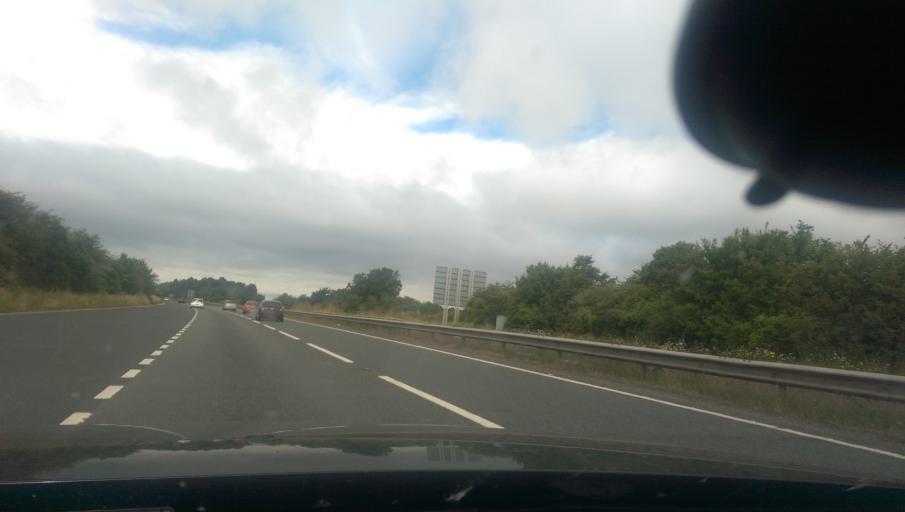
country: GB
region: England
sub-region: Hampshire
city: Abbotts Ann
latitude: 51.2129
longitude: -1.5234
